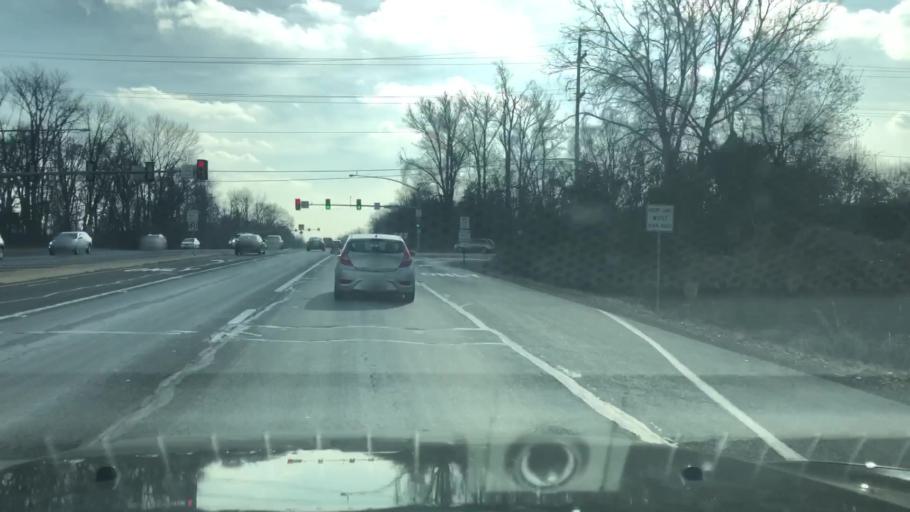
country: US
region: Pennsylvania
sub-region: Bucks County
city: Newtown
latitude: 40.2271
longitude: -74.9480
